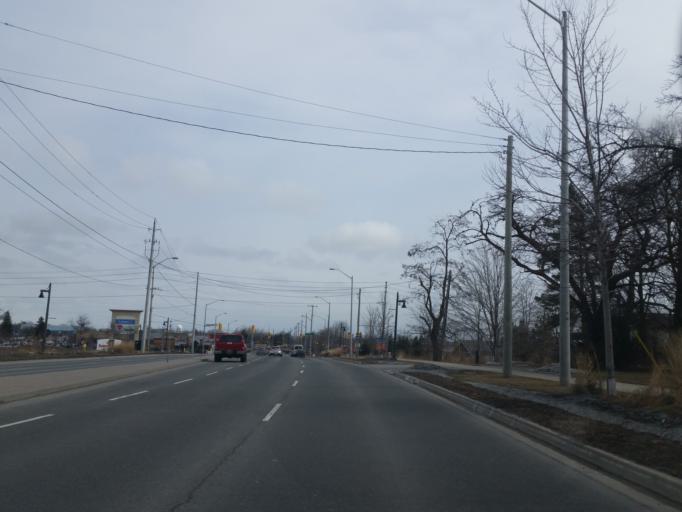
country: CA
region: Ontario
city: Oshawa
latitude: 43.9093
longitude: -78.7143
